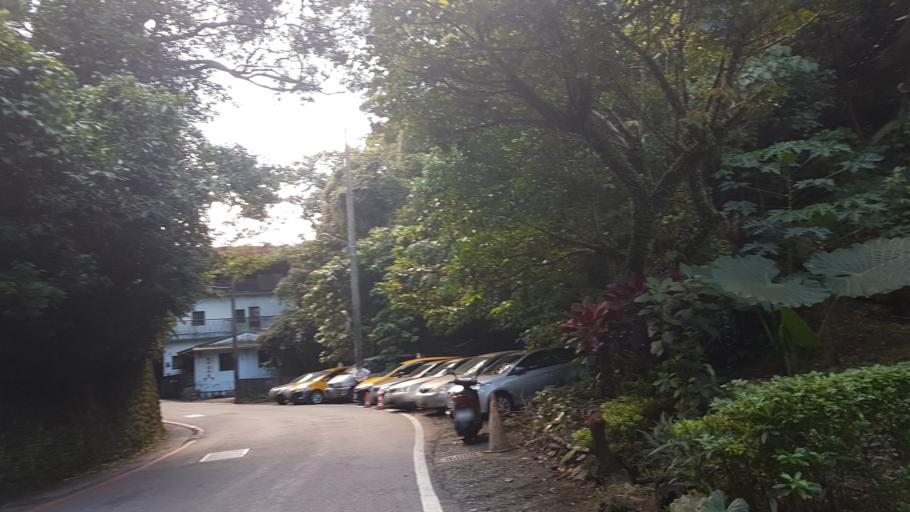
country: TW
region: Taipei
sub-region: Taipei
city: Banqiao
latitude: 24.9515
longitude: 121.5310
